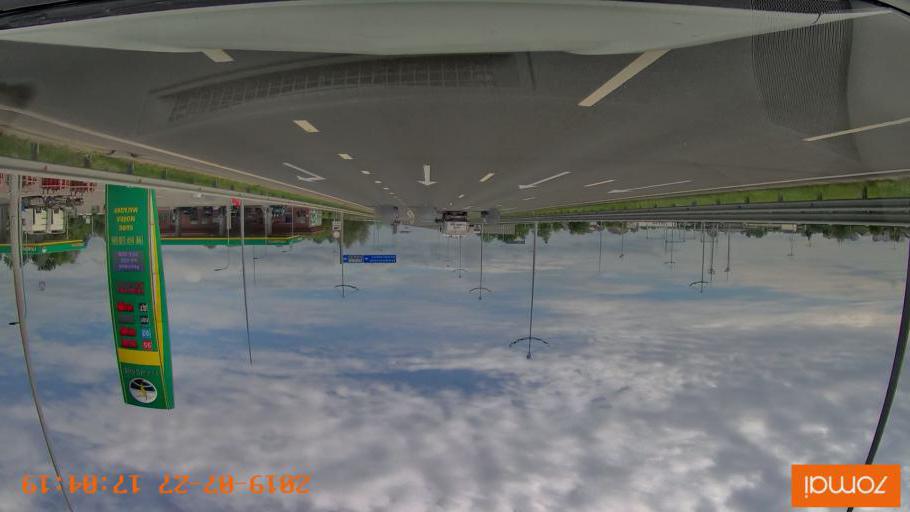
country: RU
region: Kaliningrad
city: Bol'shoe Isakovo
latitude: 54.7128
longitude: 20.5970
